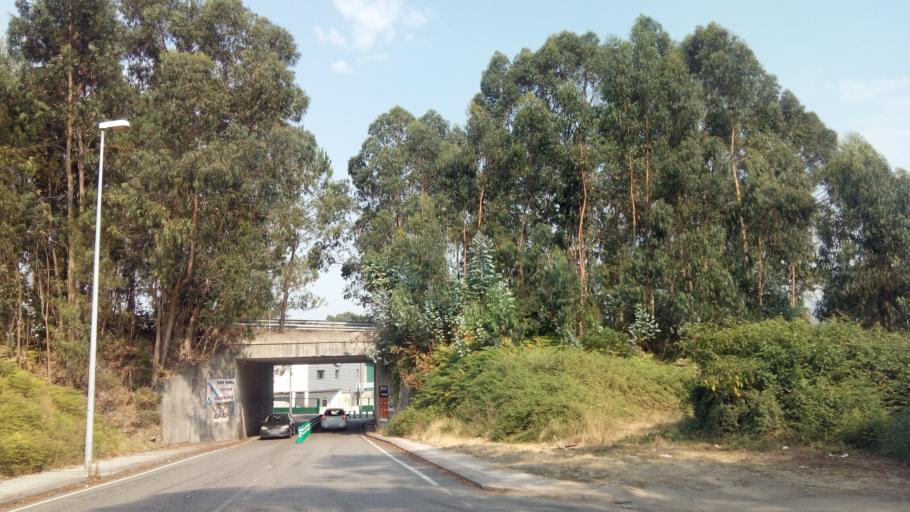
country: PT
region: Viana do Castelo
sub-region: Valenca
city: Valenca
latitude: 42.0373
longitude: -8.6628
